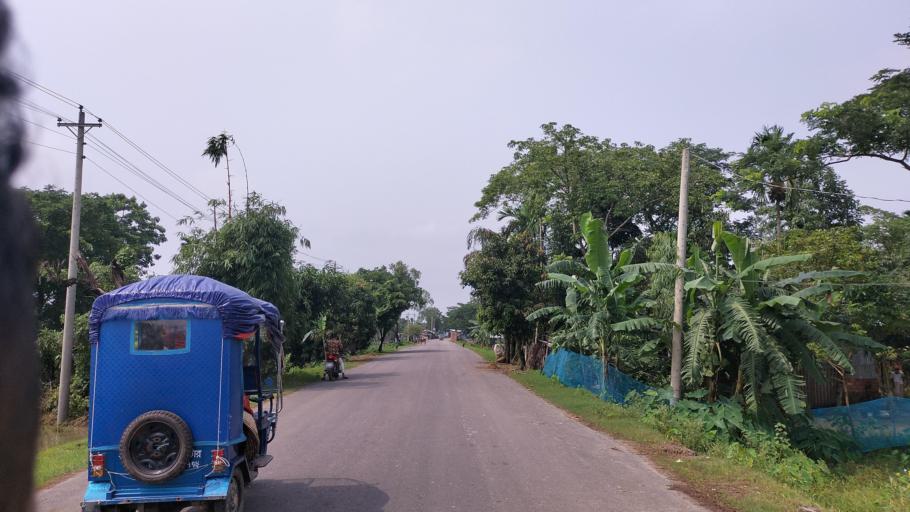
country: BD
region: Dhaka
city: Netrakona
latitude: 24.9495
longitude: 90.8323
